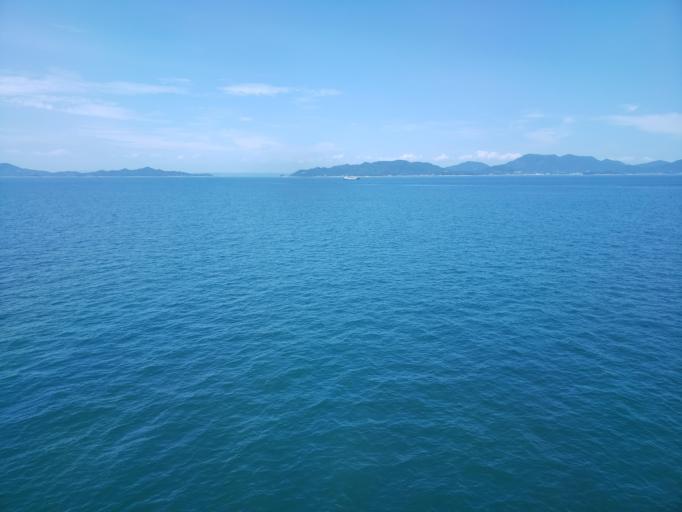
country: JP
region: Kagawa
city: Tonosho
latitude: 34.4058
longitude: 134.1528
